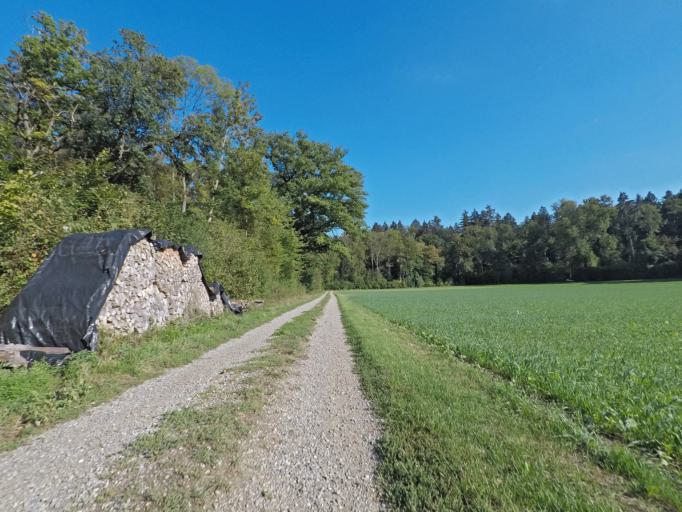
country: CH
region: Thurgau
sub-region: Frauenfeld District
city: Diessenhofen
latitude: 47.6571
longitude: 8.7401
